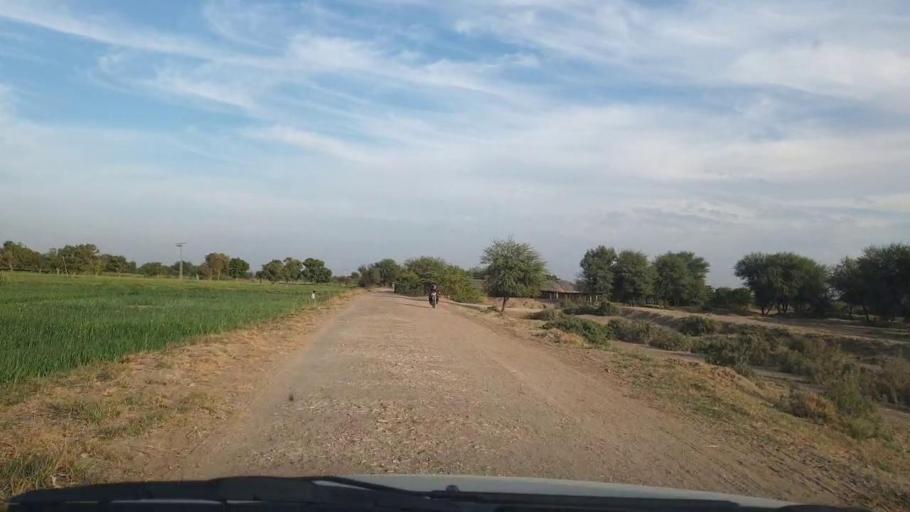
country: PK
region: Sindh
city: Pithoro
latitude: 25.6436
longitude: 69.2768
